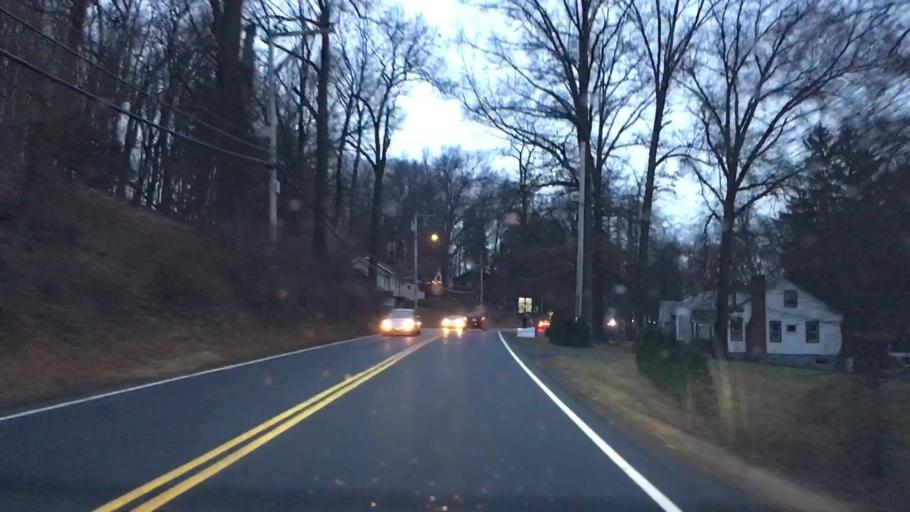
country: US
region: New York
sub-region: Dutchess County
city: Red Oaks Mill
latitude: 41.6567
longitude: -73.8684
